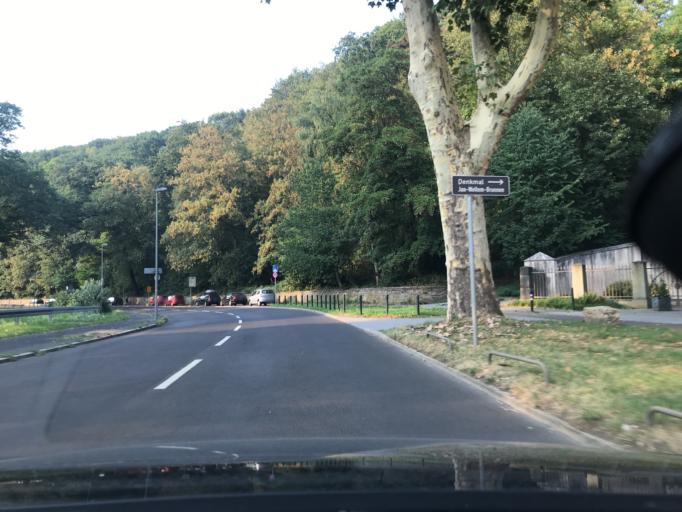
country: DE
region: North Rhine-Westphalia
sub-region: Regierungsbezirk Dusseldorf
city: Ratingen
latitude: 51.2425
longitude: 6.8306
